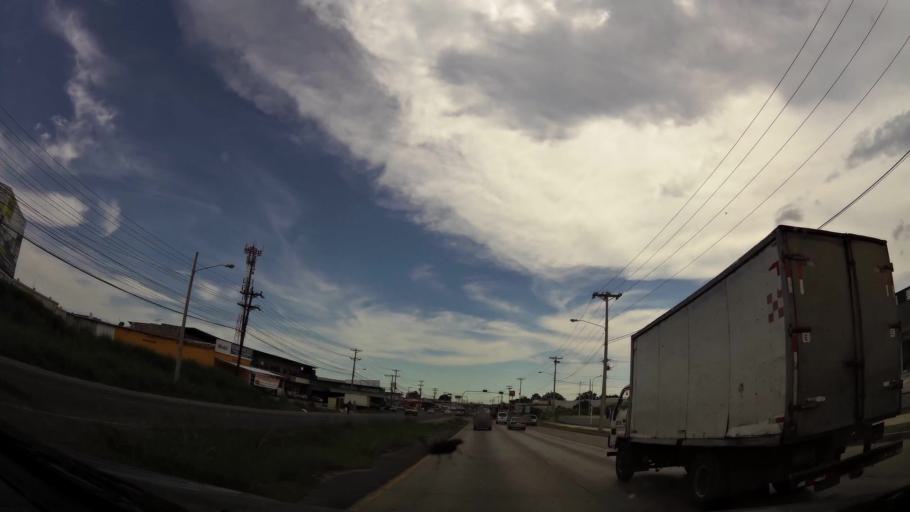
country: PA
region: Panama
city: Tocumen
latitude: 9.0857
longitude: -79.3976
